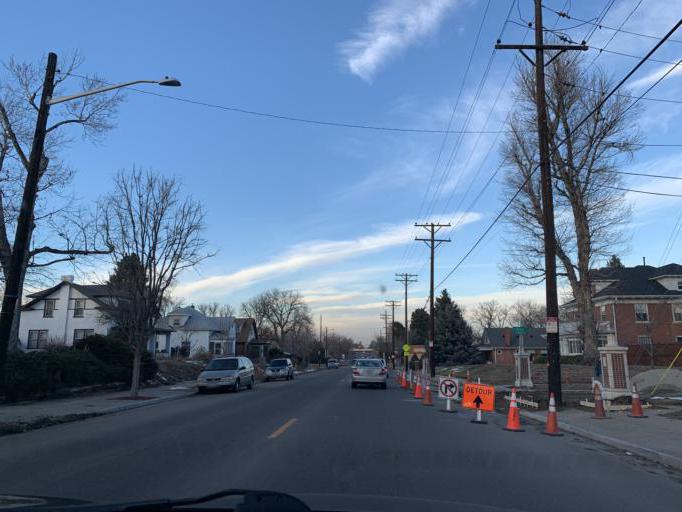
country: US
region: Colorado
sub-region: Adams County
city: Berkley
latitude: 39.7788
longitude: -105.0346
